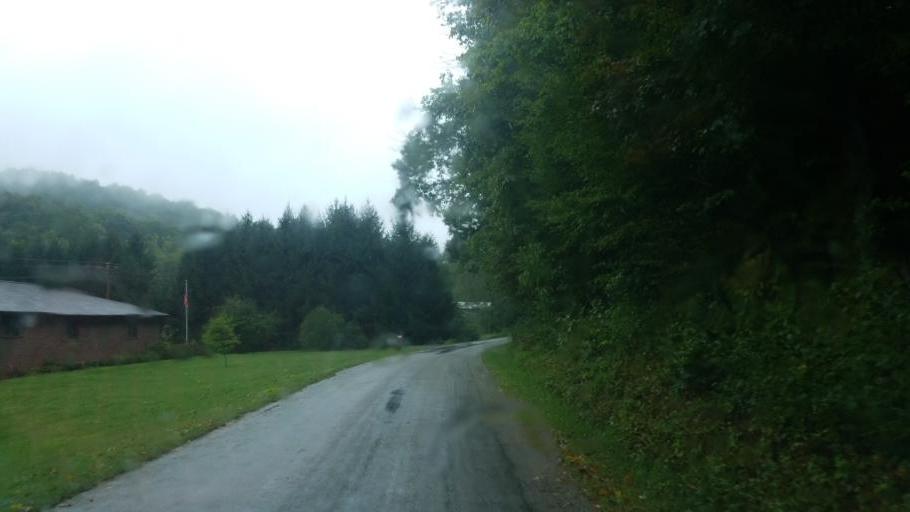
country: US
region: Kentucky
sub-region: Lewis County
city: Vanceburg
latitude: 38.7875
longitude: -83.2571
